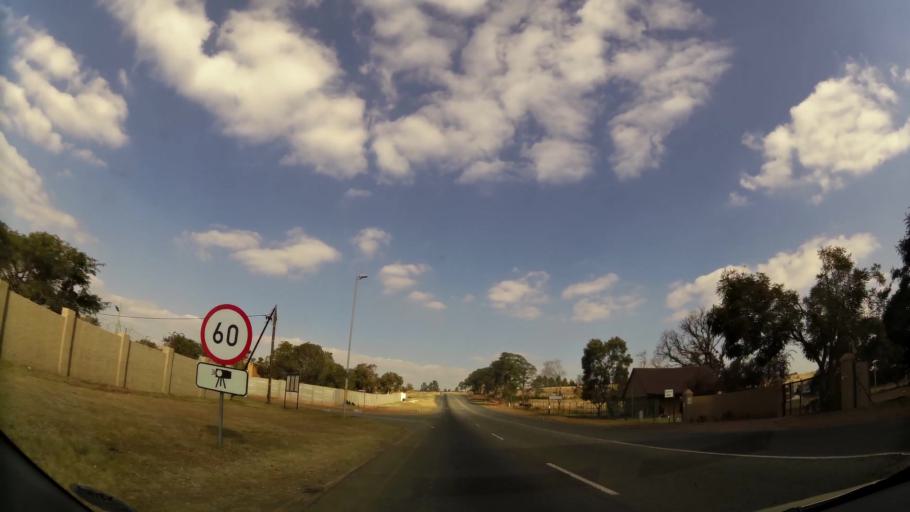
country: ZA
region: Gauteng
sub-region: West Rand District Municipality
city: Krugersdorp
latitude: -26.0523
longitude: 27.7541
